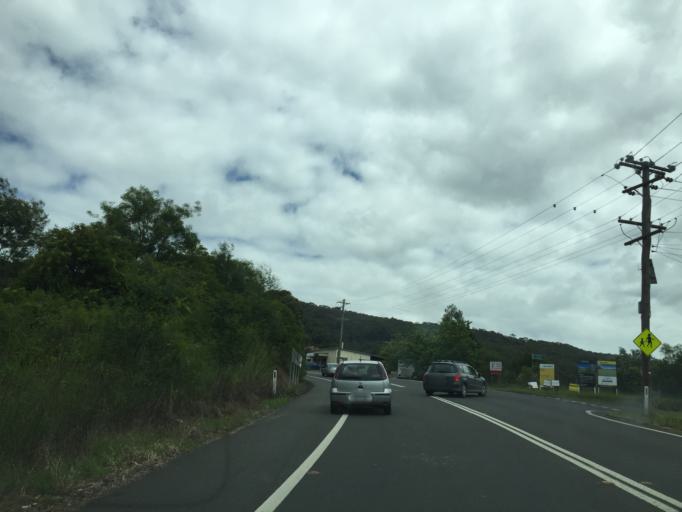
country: AU
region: New South Wales
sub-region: Hawkesbury
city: Richmond
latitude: -33.5428
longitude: 150.6456
